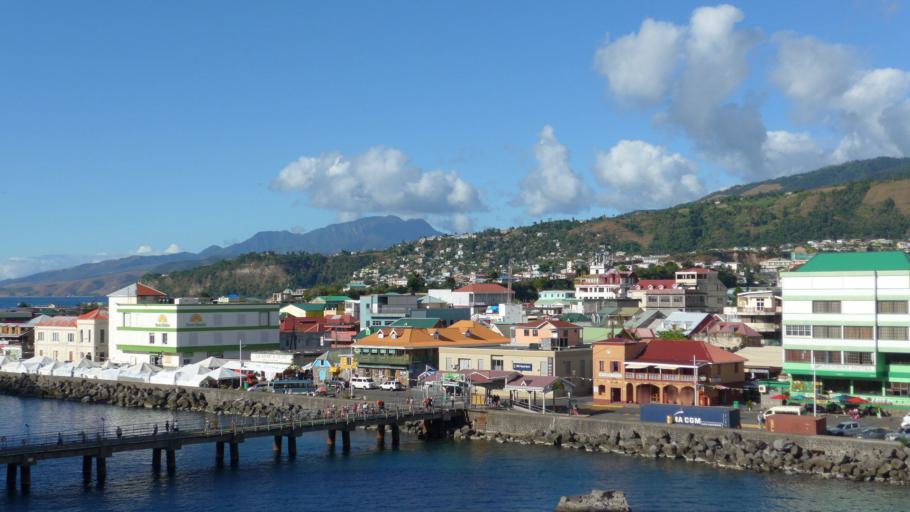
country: DM
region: Saint George
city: Roseau
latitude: 15.2950
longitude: -61.3880
